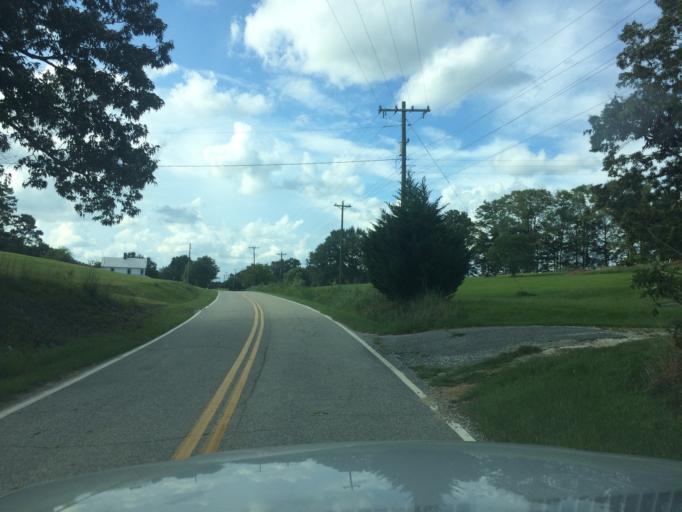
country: US
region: South Carolina
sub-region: Spartanburg County
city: Woodruff
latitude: 34.7611
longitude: -82.1021
